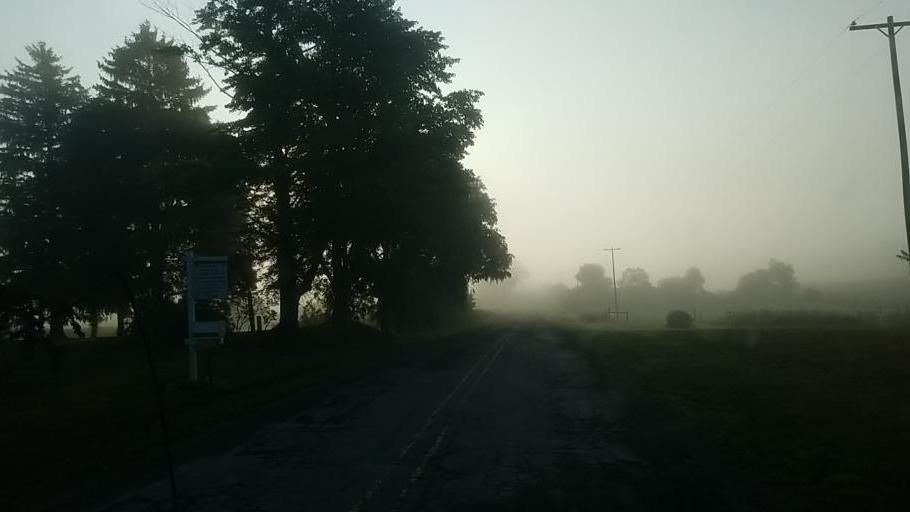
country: US
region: Michigan
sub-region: Newaygo County
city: Fremont
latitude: 43.4529
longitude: -86.0464
